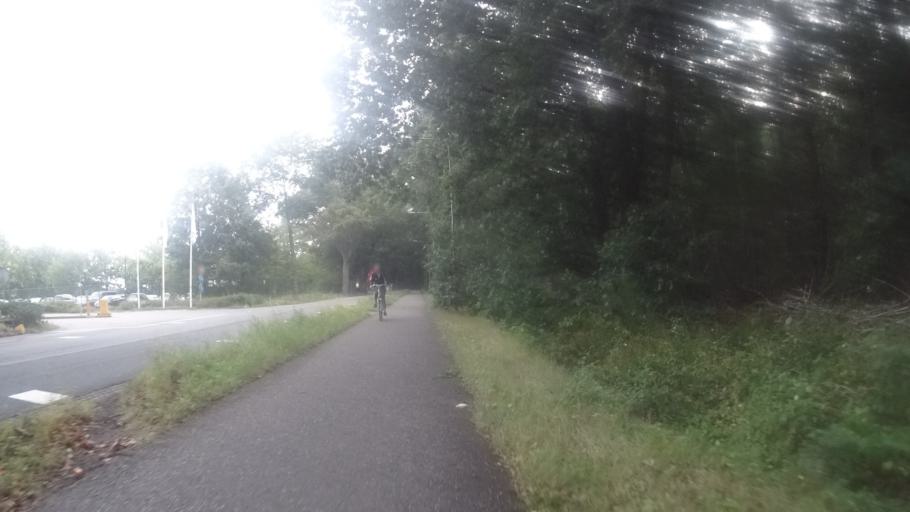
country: NL
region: Limburg
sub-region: Gemeente Venlo
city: Venlo
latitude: 51.4018
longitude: 6.1629
